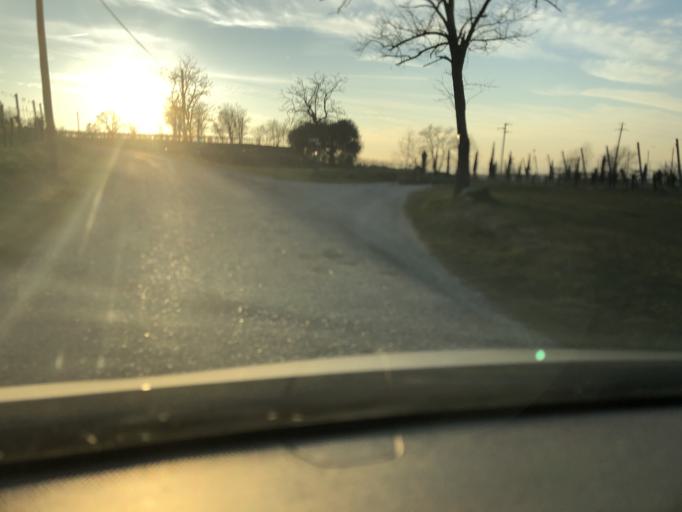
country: IT
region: Veneto
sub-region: Provincia di Verona
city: Pastrengo
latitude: 45.4748
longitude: 10.8086
